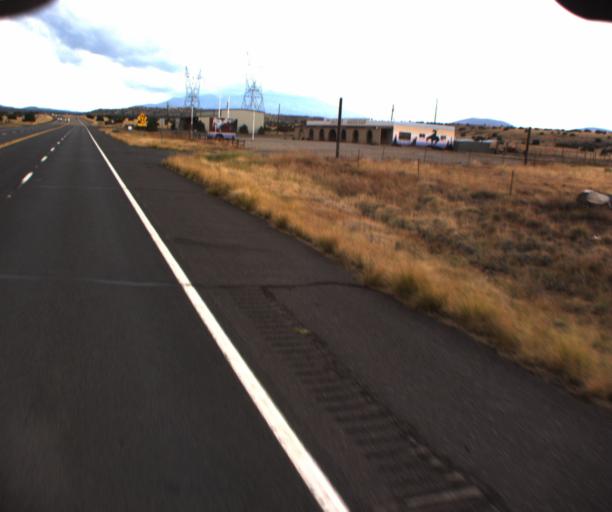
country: US
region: Arizona
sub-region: Coconino County
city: Flagstaff
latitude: 35.5418
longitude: -111.5389
